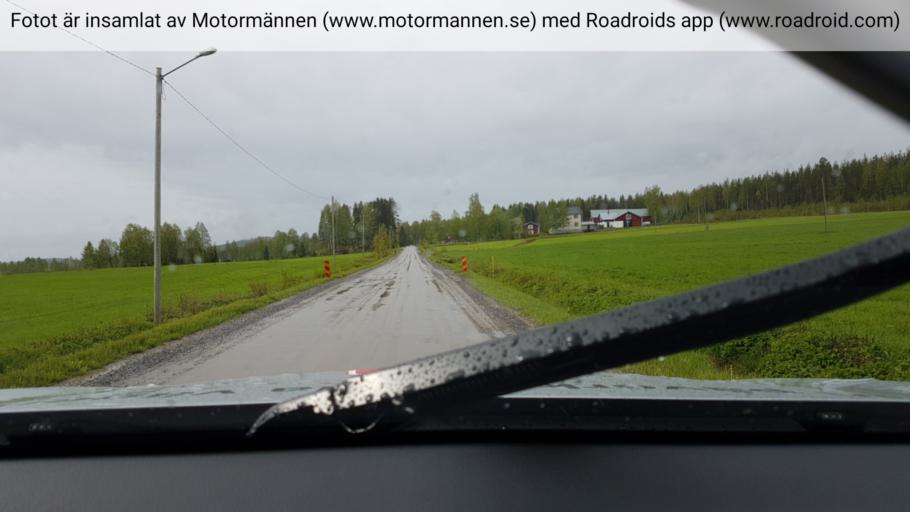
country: SE
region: Vaesterbotten
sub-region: Vannas Kommun
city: Vaennaes
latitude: 63.8332
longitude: 19.6313
